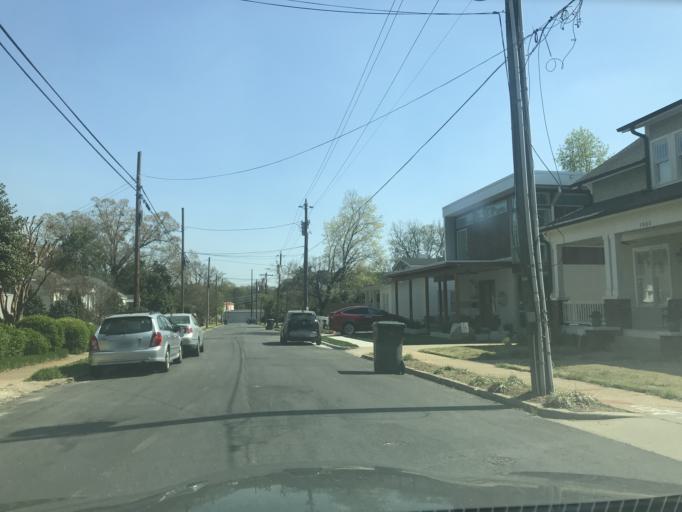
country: US
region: North Carolina
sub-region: Wake County
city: Raleigh
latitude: 35.8039
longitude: -78.6367
